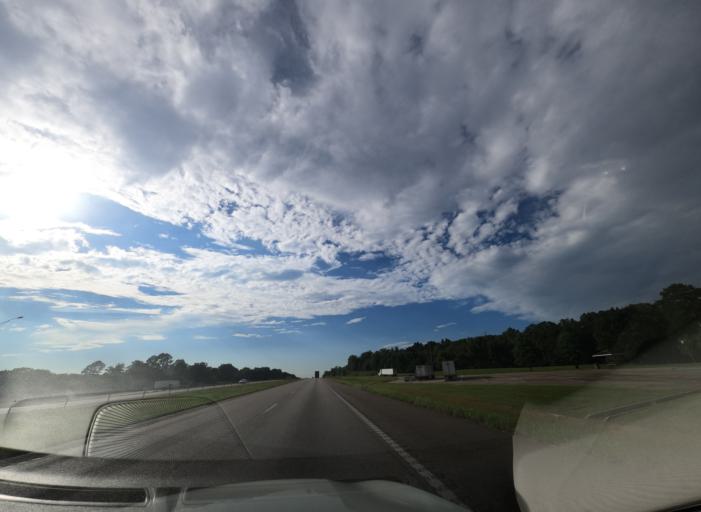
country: US
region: Missouri
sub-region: Sainte Genevieve County
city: Sainte Genevieve
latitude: 38.0308
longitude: -90.2490
